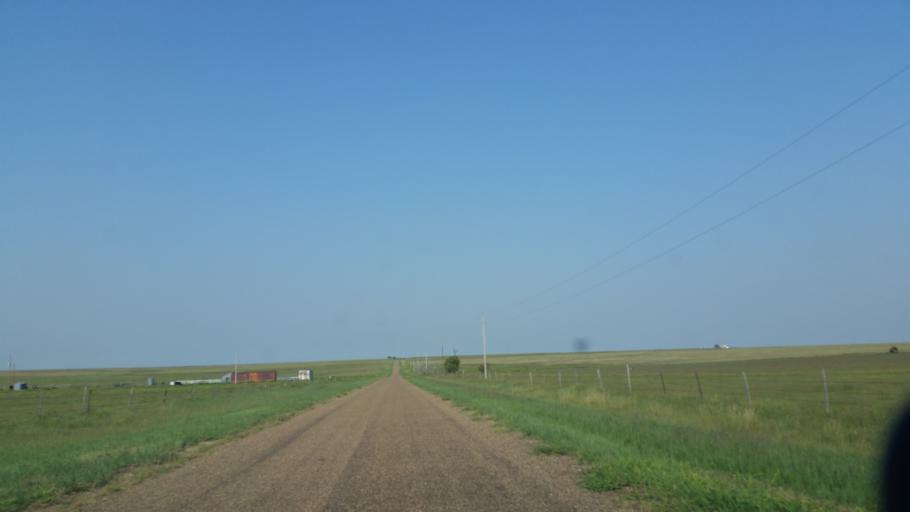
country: US
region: New Mexico
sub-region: Quay County
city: Logan
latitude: 34.9082
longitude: -103.2012
